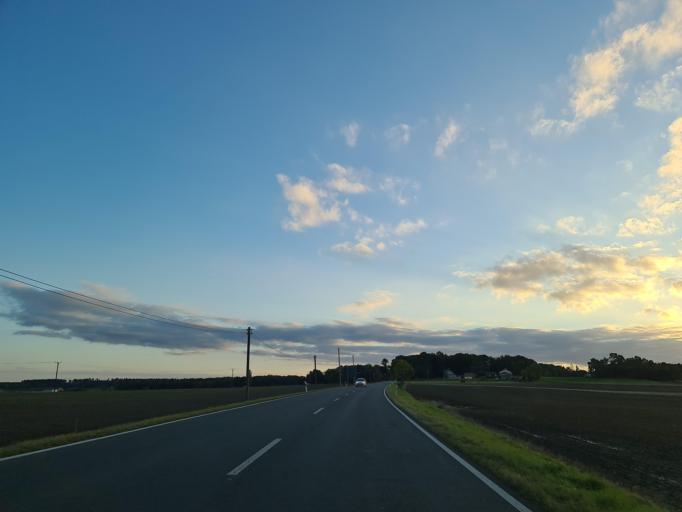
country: DE
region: Saxony
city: Syrau
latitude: 50.5580
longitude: 12.1231
